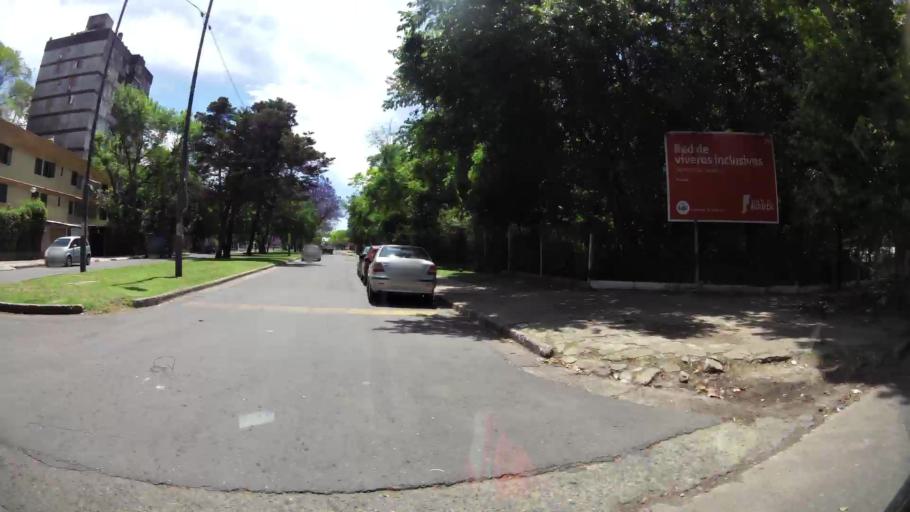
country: AR
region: Santa Fe
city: Gobernador Galvez
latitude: -32.9964
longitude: -60.6251
